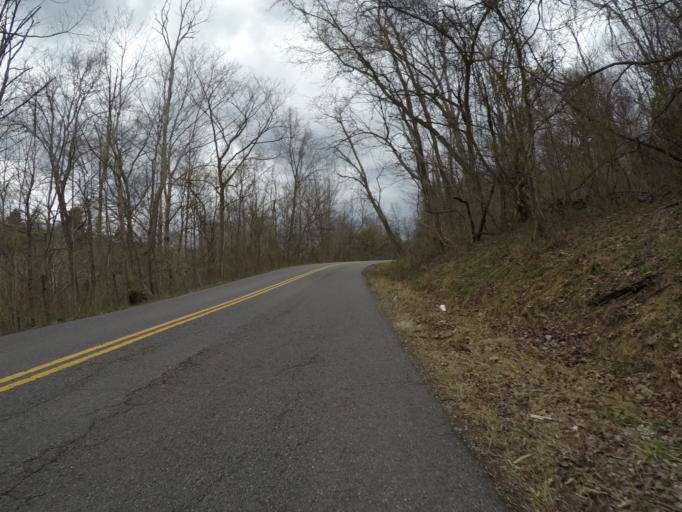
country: US
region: Ohio
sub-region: Lawrence County
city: Burlington
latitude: 38.4307
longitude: -82.5264
